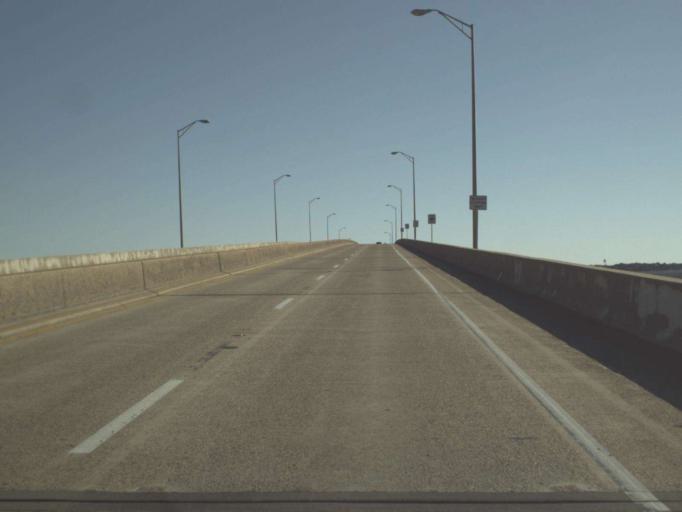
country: US
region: Florida
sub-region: Escambia County
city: East Pensacola Heights
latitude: 30.3972
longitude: -87.1861
